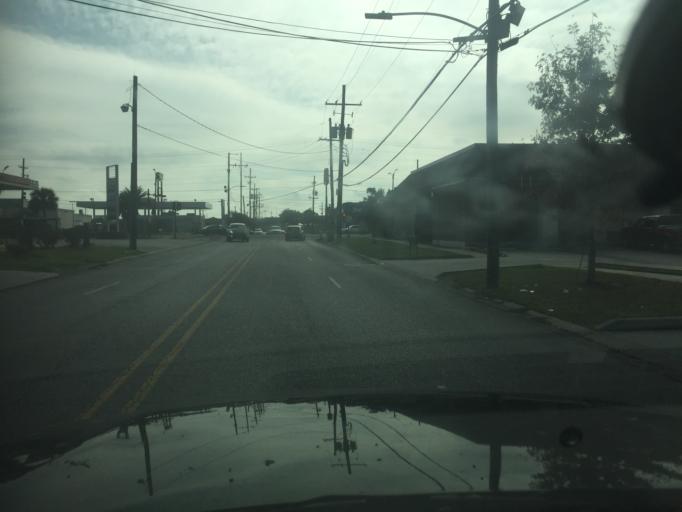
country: US
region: Louisiana
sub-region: Saint Bernard Parish
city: Arabi
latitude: 30.0061
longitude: -90.0367
